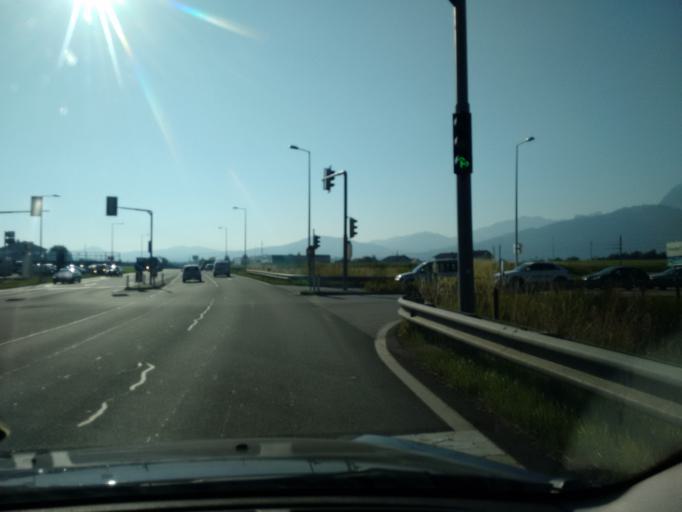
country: AT
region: Upper Austria
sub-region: Politischer Bezirk Gmunden
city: Gmunden
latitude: 47.9325
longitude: 13.7775
